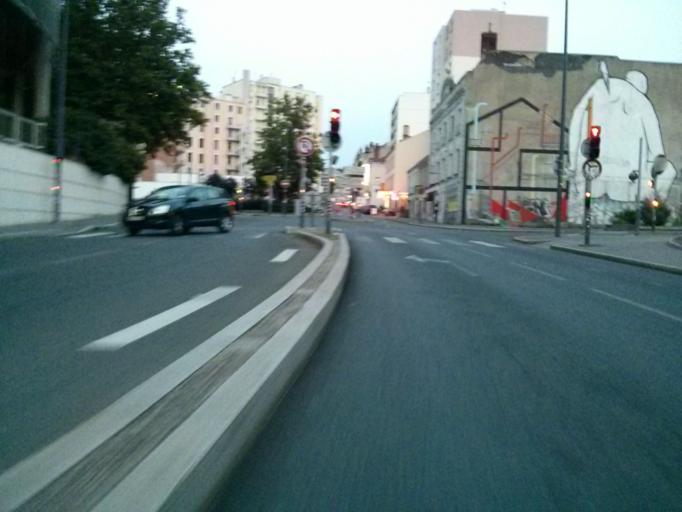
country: FR
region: Rhone-Alpes
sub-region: Departement de la Loire
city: Saint-Etienne
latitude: 45.4434
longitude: 4.3971
